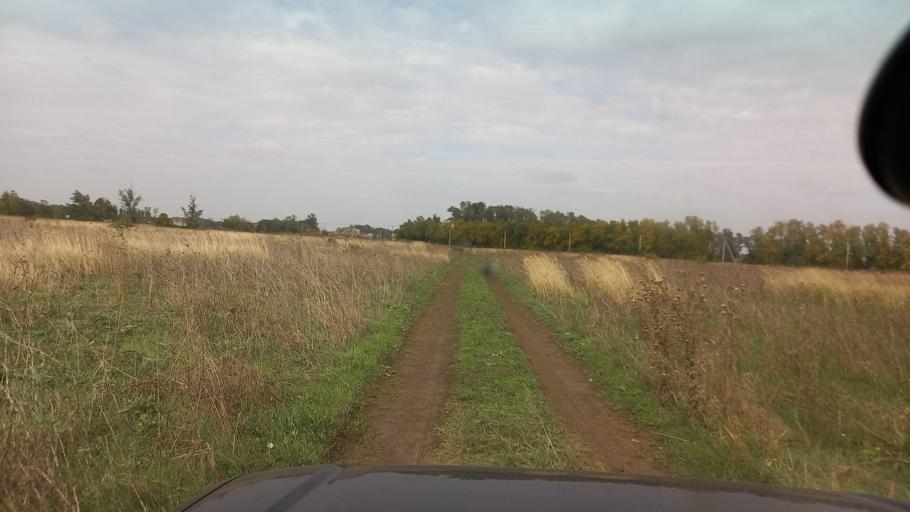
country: RU
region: Krasnodarskiy
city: Krasnodar
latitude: 45.1286
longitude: 38.9193
